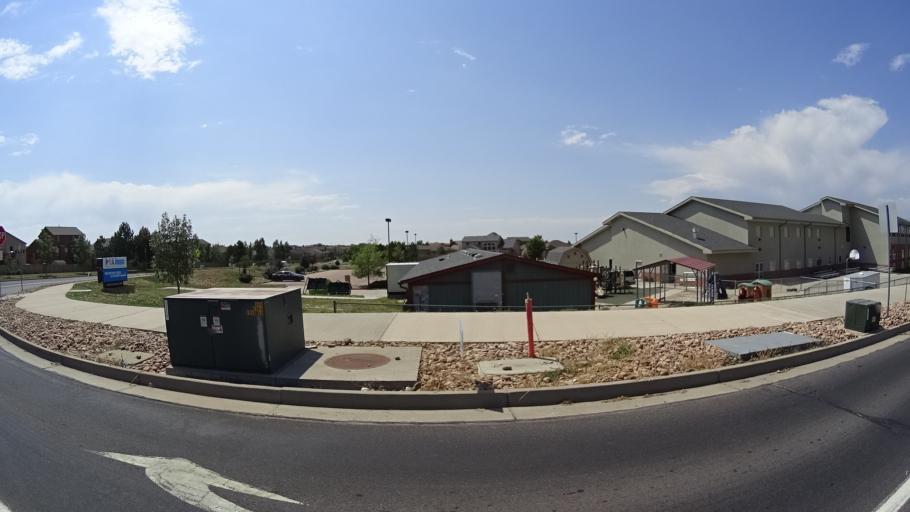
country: US
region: Colorado
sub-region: El Paso County
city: Cimarron Hills
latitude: 38.9261
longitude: -104.6930
